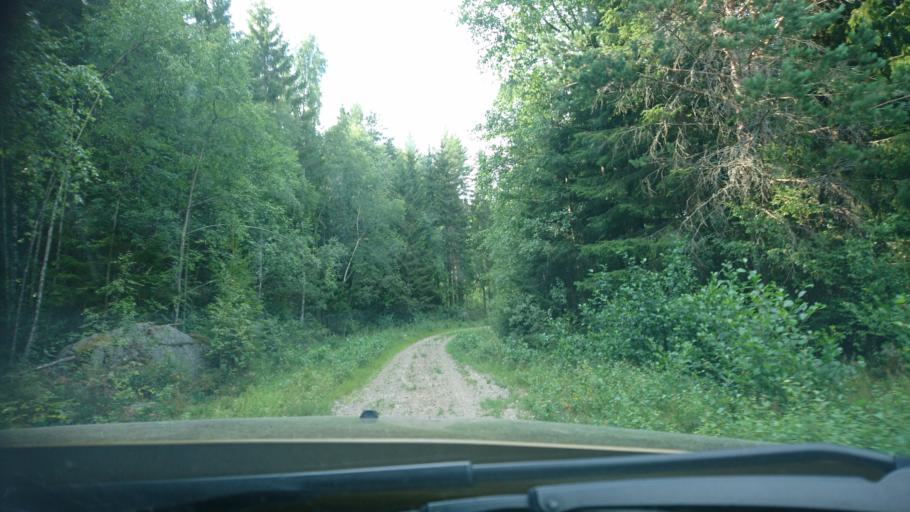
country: SE
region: Vaermland
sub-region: Kristinehamns Kommun
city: Bjorneborg
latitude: 59.2986
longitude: 14.3081
